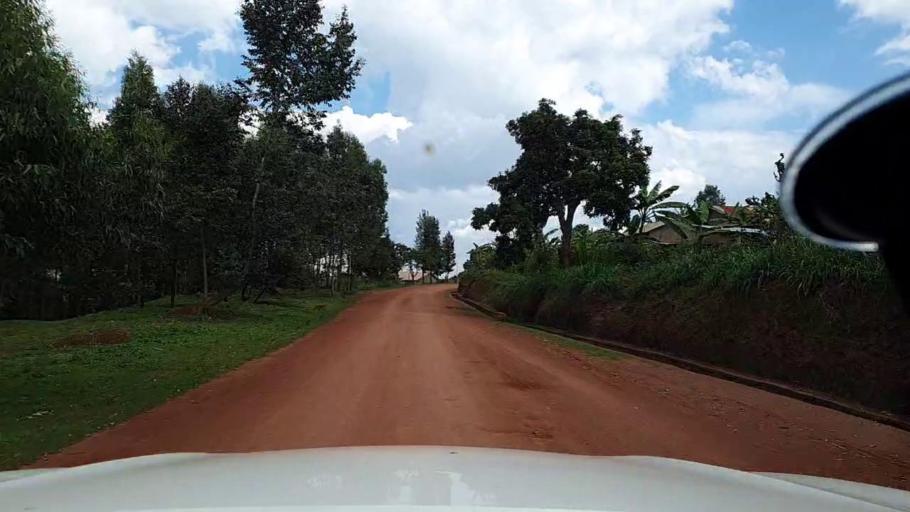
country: RW
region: Kigali
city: Kigali
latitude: -1.8093
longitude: 29.8431
